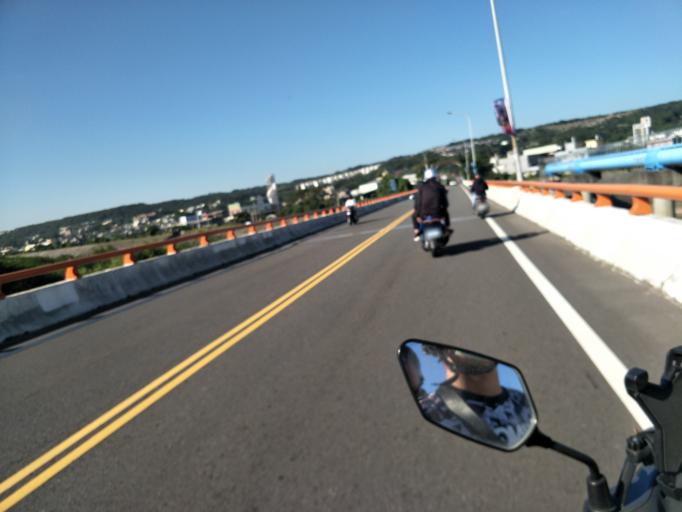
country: TW
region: Taiwan
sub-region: Hsinchu
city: Zhubei
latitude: 24.8371
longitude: 121.0363
